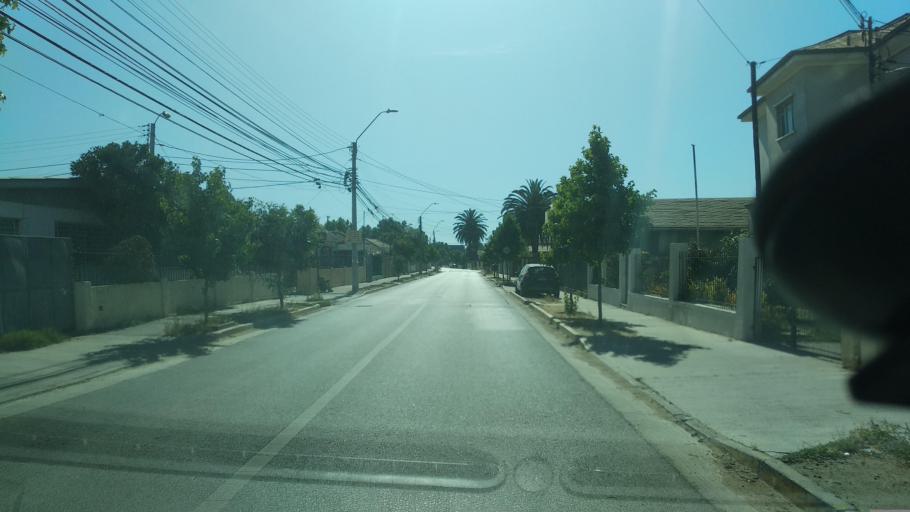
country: CL
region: Valparaiso
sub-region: Provincia de Marga Marga
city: Villa Alemana
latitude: -33.0432
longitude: -71.3829
